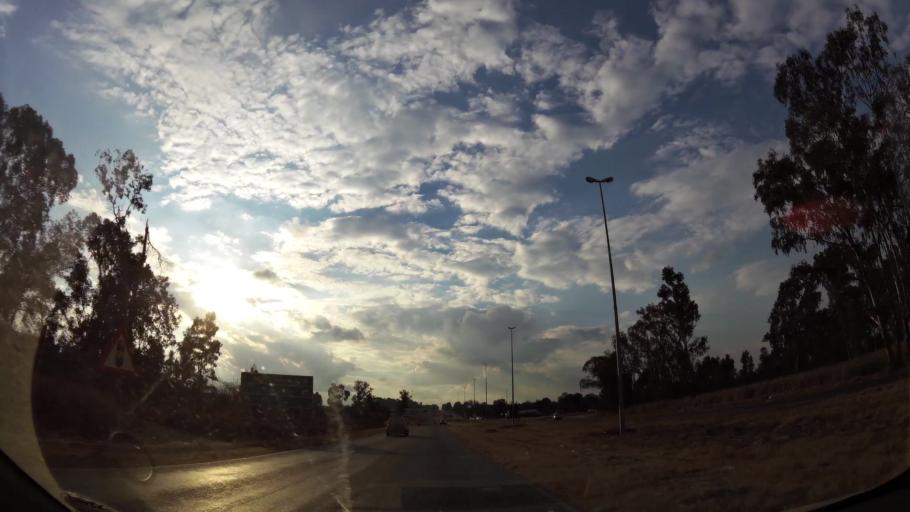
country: ZA
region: Gauteng
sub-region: Sedibeng District Municipality
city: Vanderbijlpark
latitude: -26.7117
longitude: 27.8168
